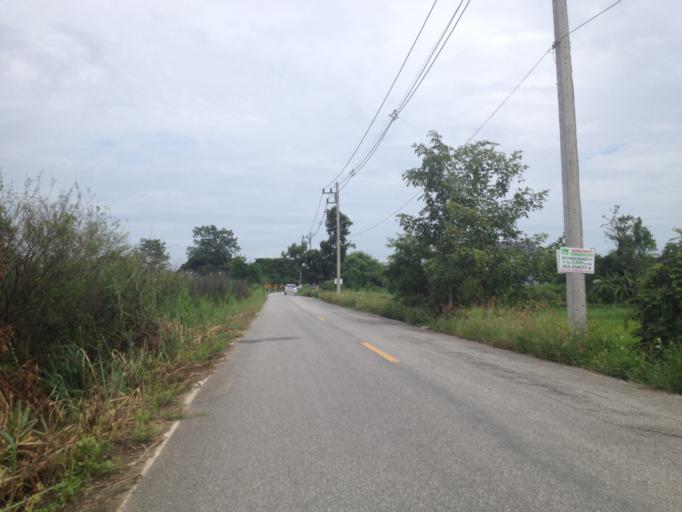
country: TH
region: Chiang Mai
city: Hang Dong
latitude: 18.7013
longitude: 98.9741
